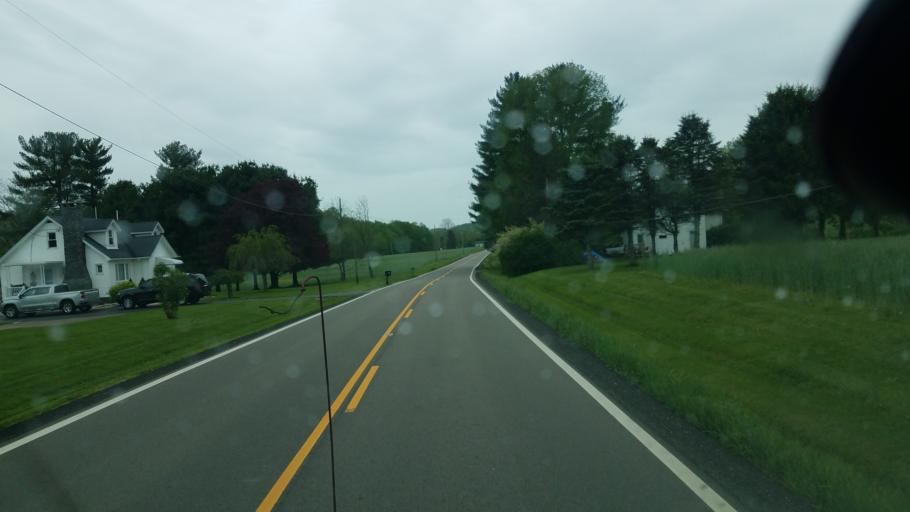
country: US
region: Ohio
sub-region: Coshocton County
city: West Lafayette
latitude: 40.2200
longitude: -81.7611
